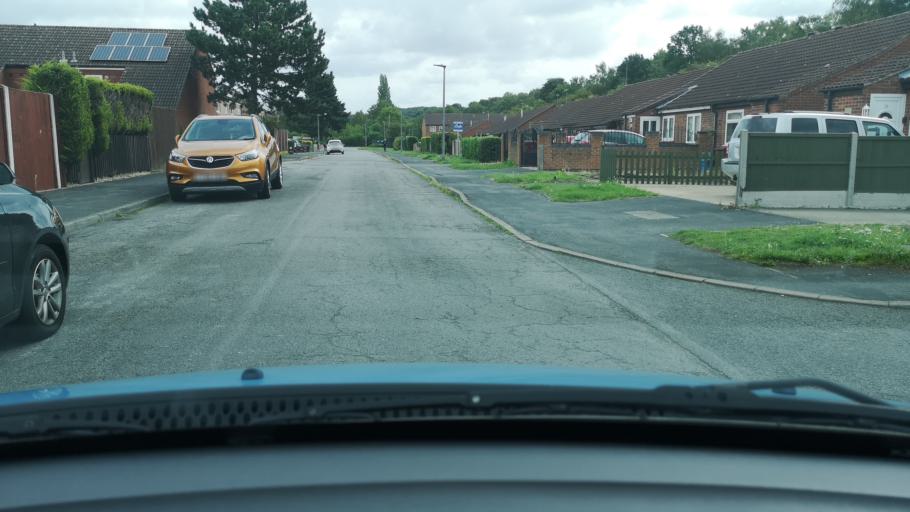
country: GB
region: England
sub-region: North Lincolnshire
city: Gunness
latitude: 53.5860
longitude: -0.6914
